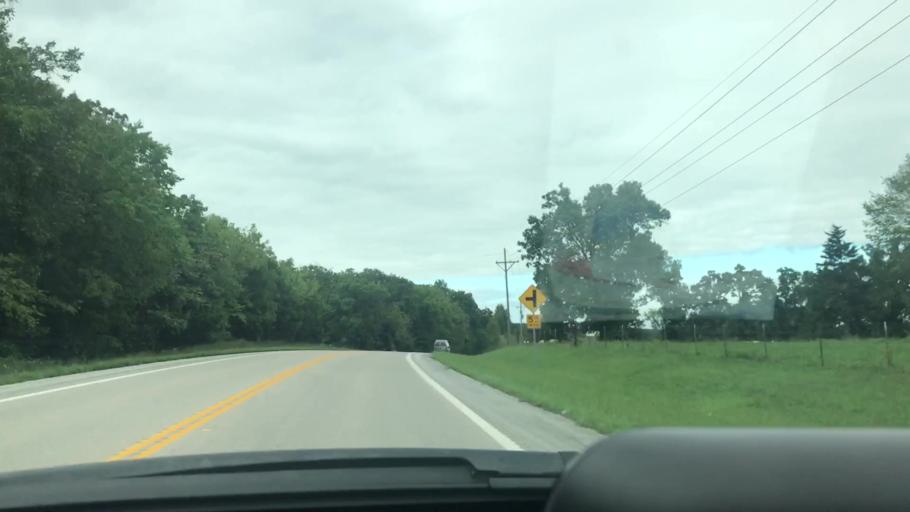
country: US
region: Missouri
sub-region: Hickory County
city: Hermitage
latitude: 37.8703
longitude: -93.1805
